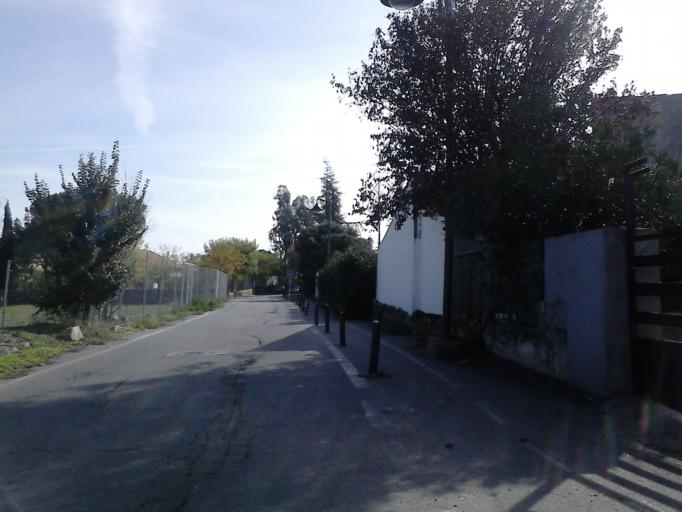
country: ES
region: Madrid
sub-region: Provincia de Madrid
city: Galapagar
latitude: 40.5776
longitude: -3.9971
